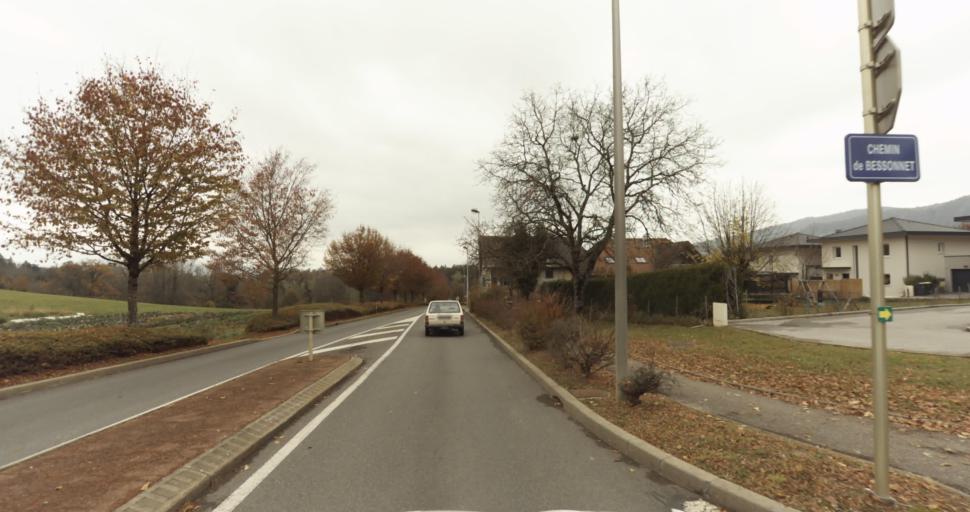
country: FR
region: Rhone-Alpes
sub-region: Departement de la Haute-Savoie
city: Seynod
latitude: 45.8638
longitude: 6.0837
